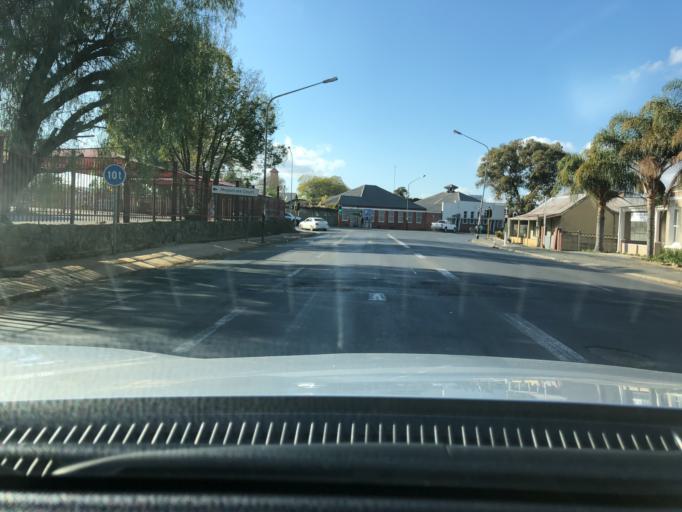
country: ZA
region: KwaZulu-Natal
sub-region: uThukela District Municipality
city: Ladysmith
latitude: -28.5597
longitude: 29.7769
